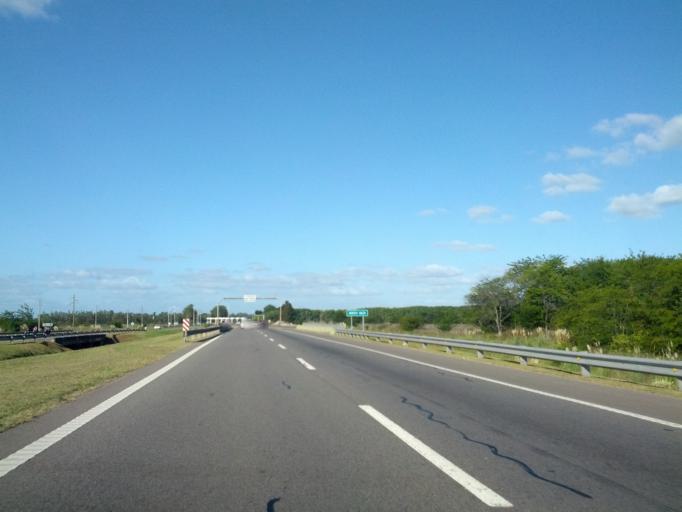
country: AR
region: Buenos Aires
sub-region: Partido de Mercedes
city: Mercedes
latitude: -34.6464
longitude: -59.3012
